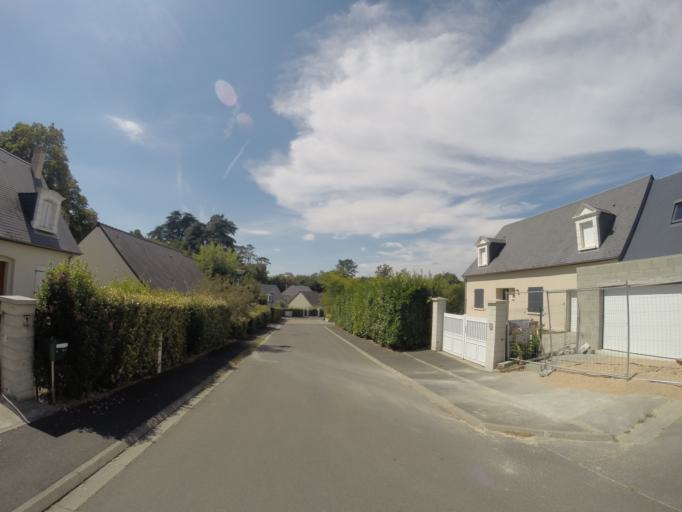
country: FR
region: Centre
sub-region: Departement d'Indre-et-Loire
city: Tours
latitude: 47.4109
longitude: 0.7086
